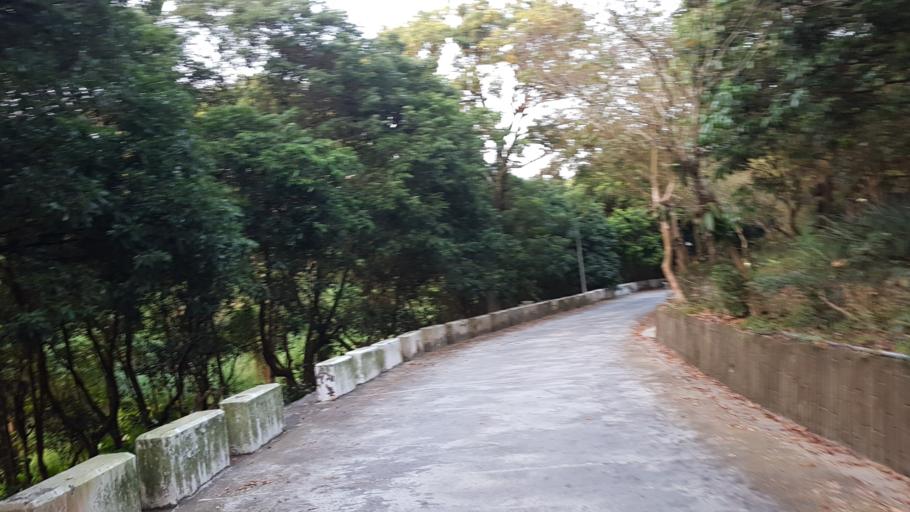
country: TW
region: Taiwan
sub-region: Chiayi
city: Jiayi Shi
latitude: 23.3595
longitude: 120.4678
